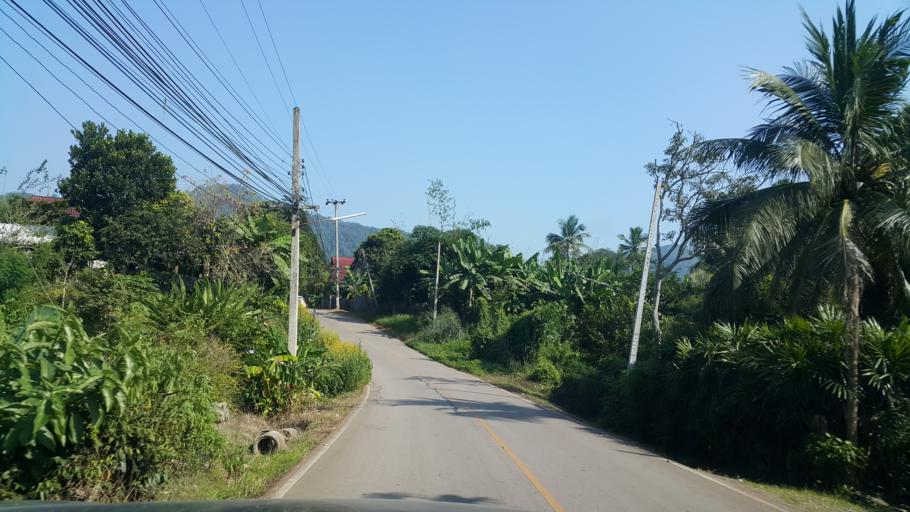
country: TH
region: Chiang Mai
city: Samoeng
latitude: 18.8543
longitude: 98.6992
